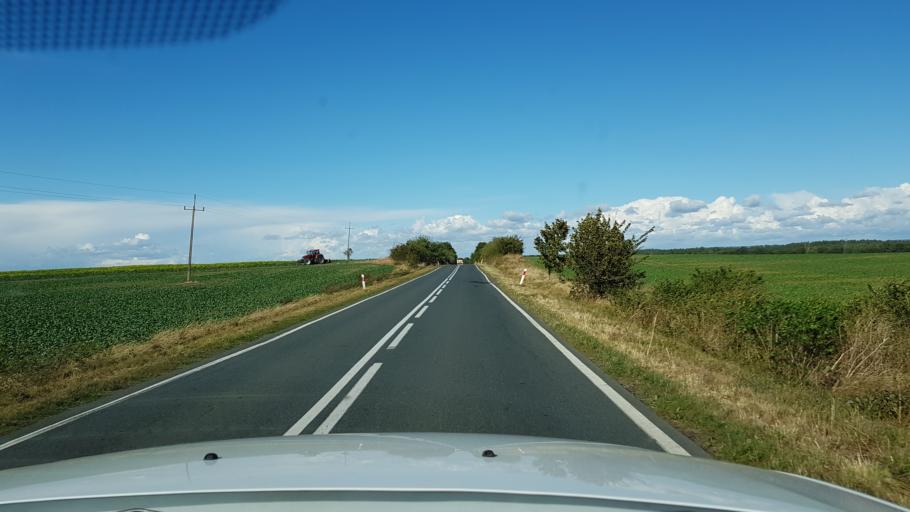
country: PL
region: West Pomeranian Voivodeship
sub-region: Powiat gryfinski
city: Banie
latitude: 53.1460
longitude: 14.6079
